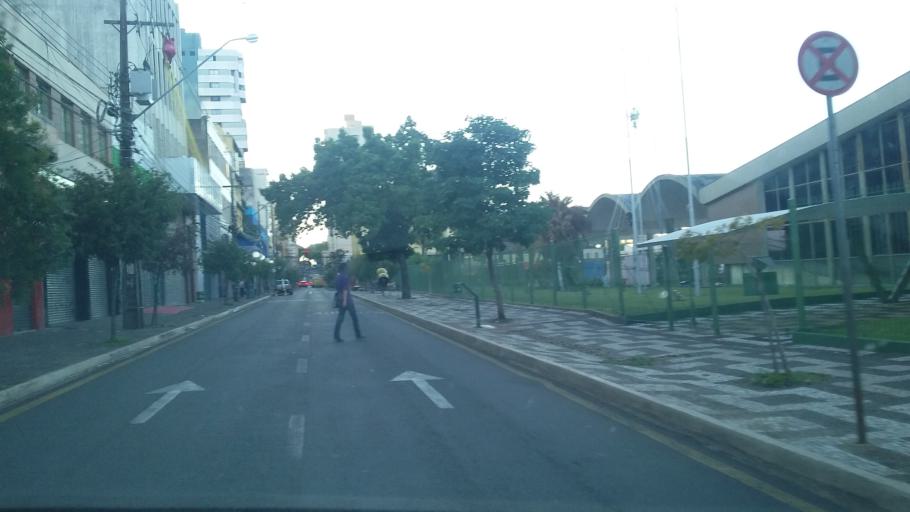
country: BR
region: Parana
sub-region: Londrina
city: Londrina
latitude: -23.3098
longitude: -51.1590
